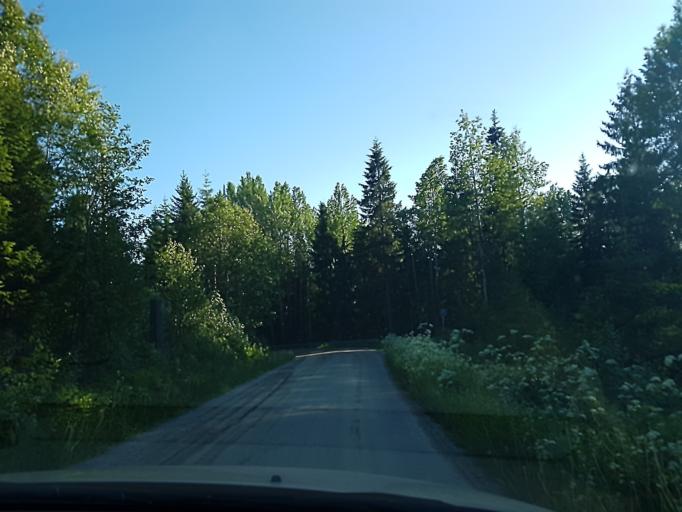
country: SE
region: Vaesternorrland
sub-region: OErnskoeldsviks Kommun
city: Bjasta
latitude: 63.0689
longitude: 18.4269
